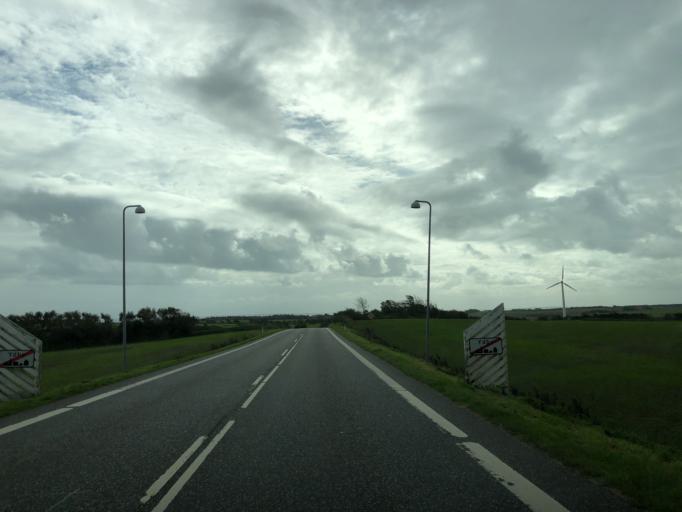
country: DK
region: North Denmark
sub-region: Thisted Kommune
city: Hurup
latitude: 56.7053
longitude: 8.4117
